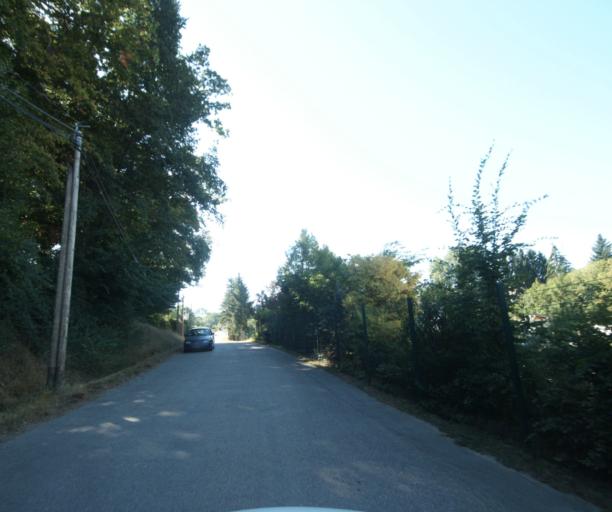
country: FR
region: Lorraine
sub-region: Departement des Vosges
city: Epinal
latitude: 48.1766
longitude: 6.4691
